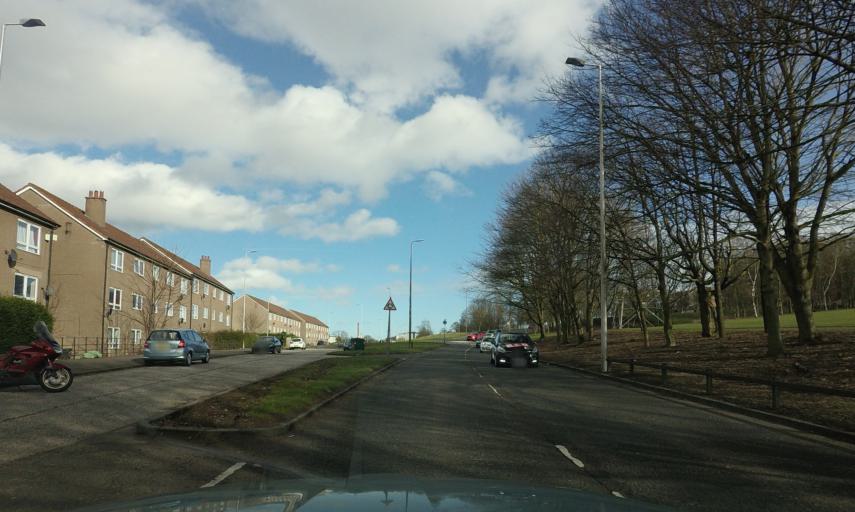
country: GB
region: Scotland
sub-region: Angus
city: Muirhead
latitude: 56.4719
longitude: -3.0337
